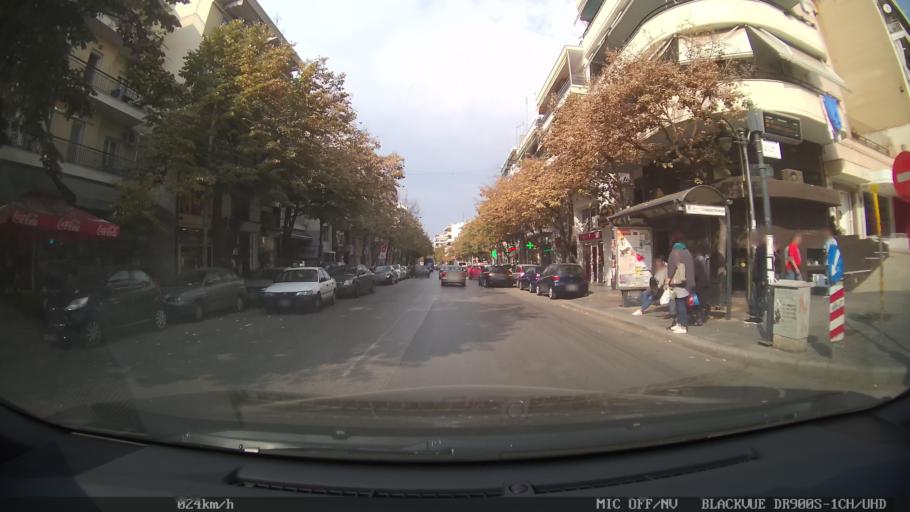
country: GR
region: Central Macedonia
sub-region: Nomos Thessalonikis
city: Triandria
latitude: 40.6135
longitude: 22.9808
